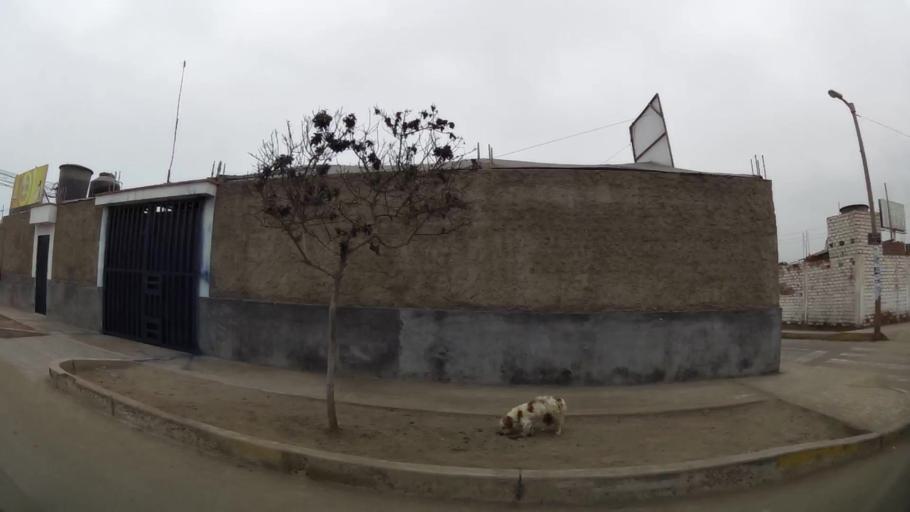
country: PE
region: Lima
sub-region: Lima
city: Punta Hermosa
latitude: -12.3092
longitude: -76.8370
